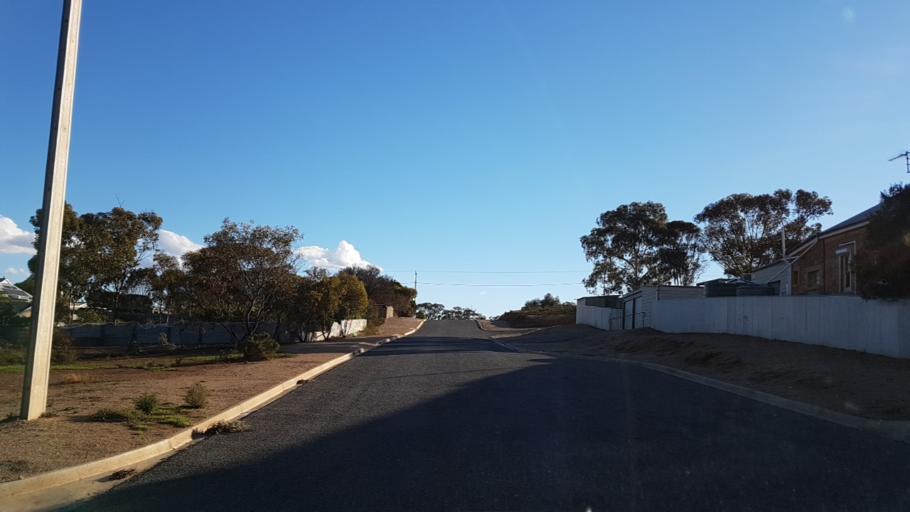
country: AU
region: South Australia
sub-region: Peterborough
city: Peterborough
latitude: -32.9690
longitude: 138.8374
